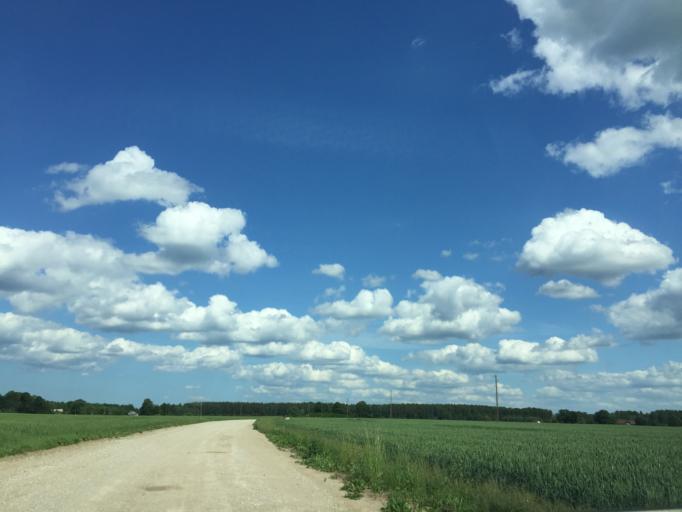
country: LV
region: Engure
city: Smarde
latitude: 56.8160
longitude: 23.3706
